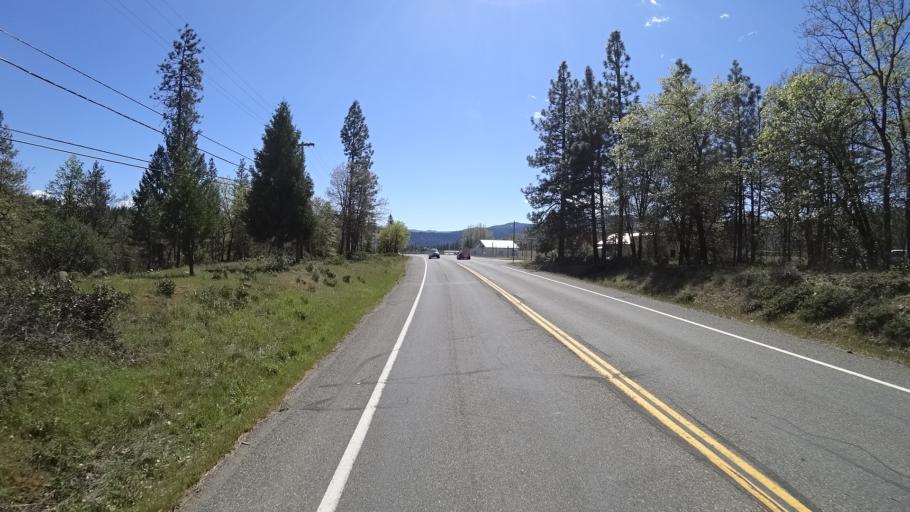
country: US
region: California
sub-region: Trinity County
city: Weaverville
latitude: 40.7483
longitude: -122.9208
